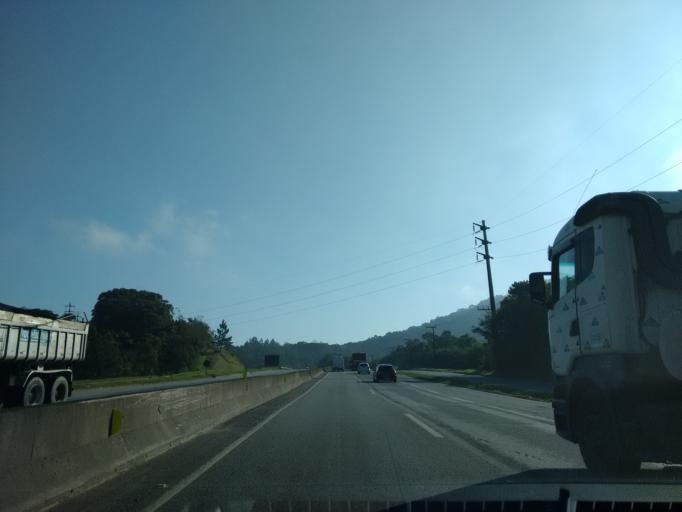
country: BR
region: Santa Catarina
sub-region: Joinville
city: Joinville
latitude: -26.3155
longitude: -48.8737
